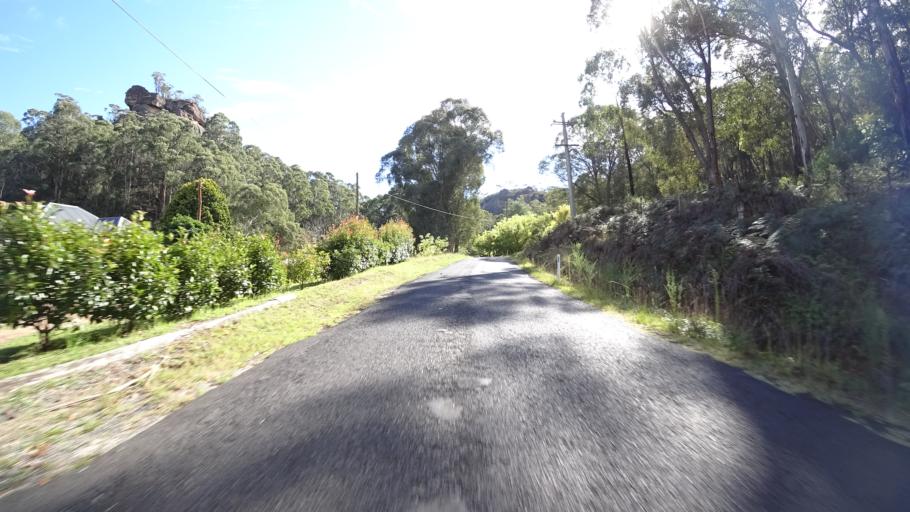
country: AU
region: New South Wales
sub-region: Lithgow
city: Lithgow
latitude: -33.4563
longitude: 150.1724
